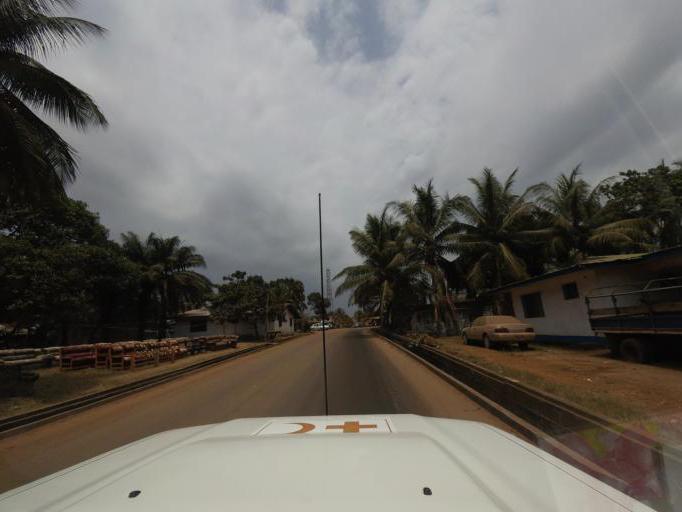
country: LR
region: Montserrado
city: Monrovia
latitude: 6.3026
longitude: -10.6867
